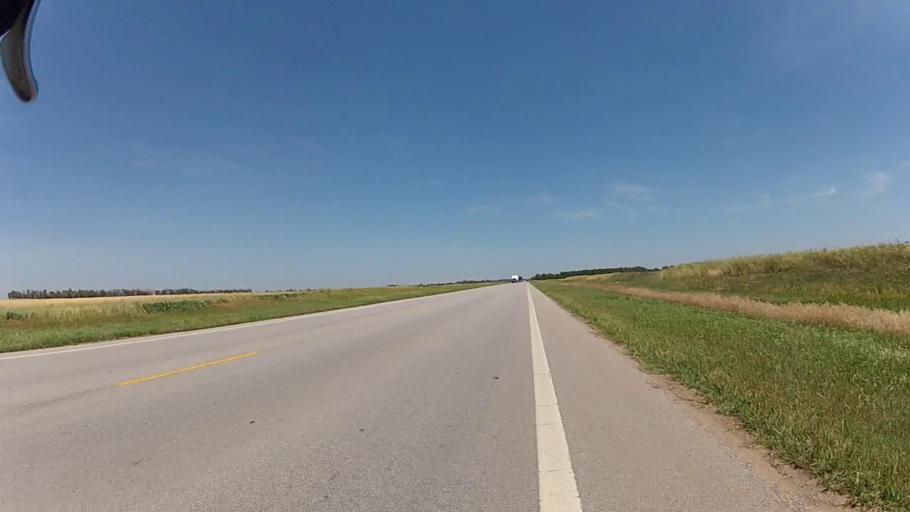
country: US
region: Kansas
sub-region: Harper County
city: Harper
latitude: 37.2389
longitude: -98.1430
